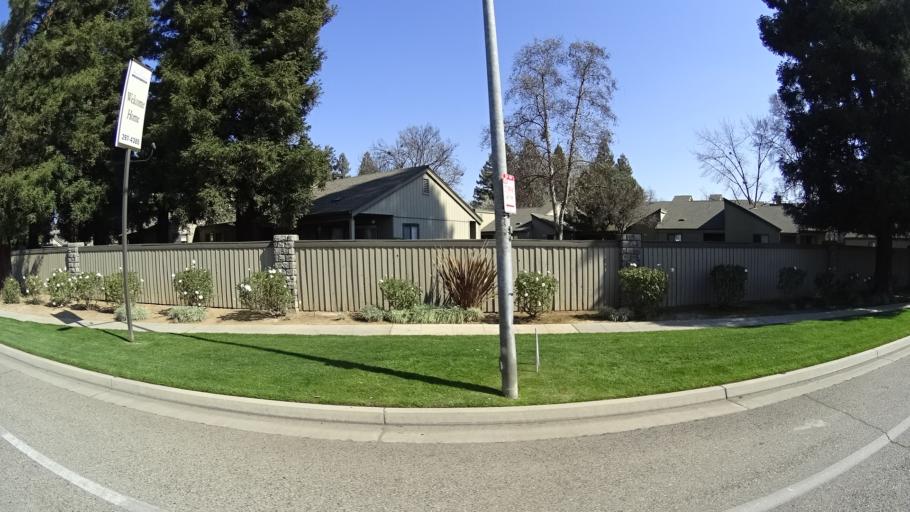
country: US
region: California
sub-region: Fresno County
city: Clovis
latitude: 36.8622
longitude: -119.7567
